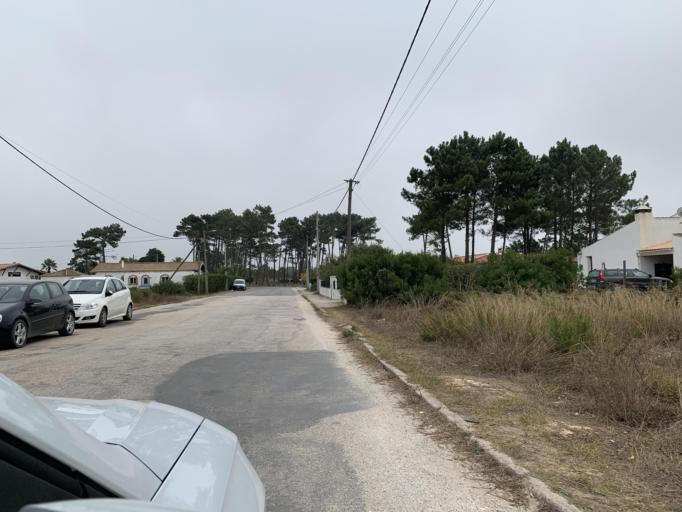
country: PT
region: Faro
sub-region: Aljezur
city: Aljezur
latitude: 37.3052
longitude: -8.8513
